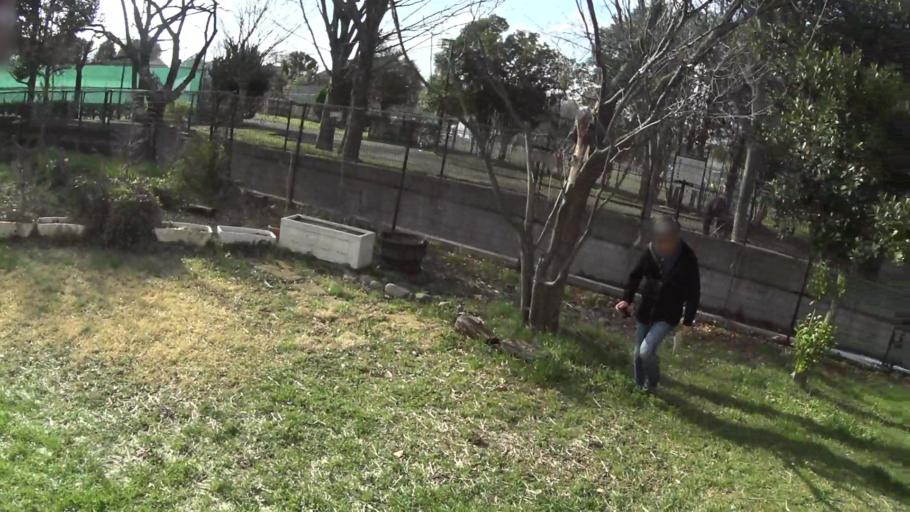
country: JP
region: Tokyo
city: Mitaka-shi
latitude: 35.6558
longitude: 139.6004
